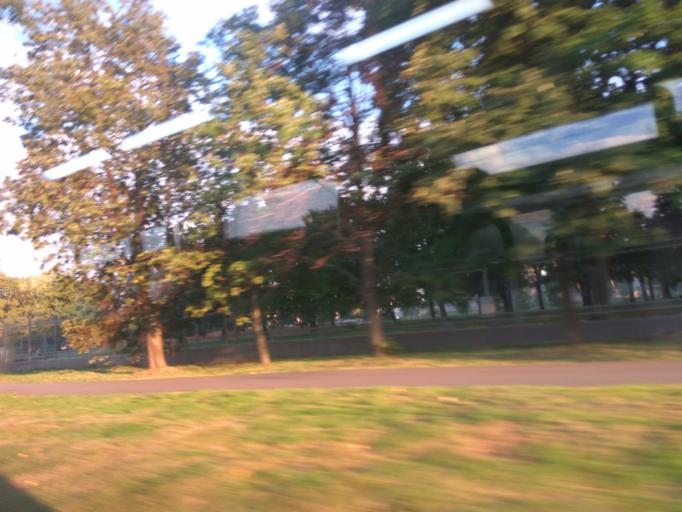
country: RU
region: Moscow
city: Ostankinskiy
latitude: 55.8214
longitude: 37.6111
